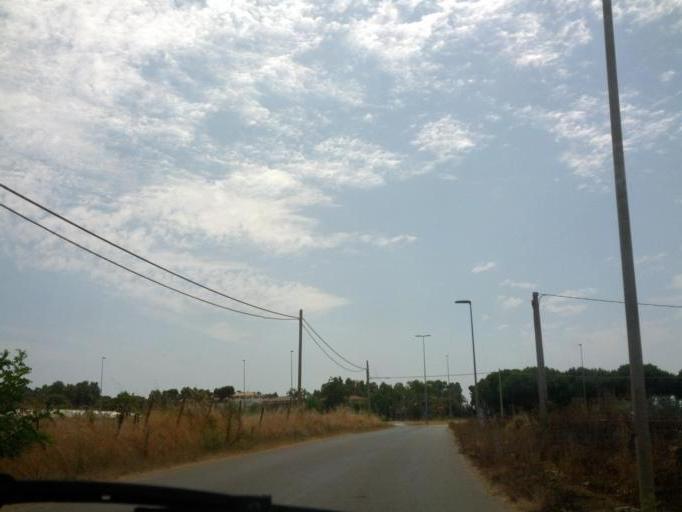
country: IT
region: Latium
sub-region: Provincia di Latina
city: Sperlonga
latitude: 41.2862
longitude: 13.3897
